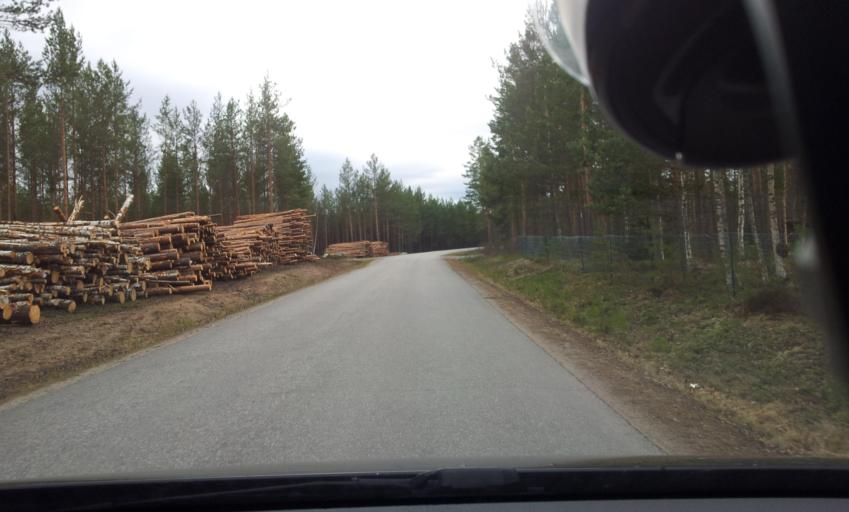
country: SE
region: Gaevleborg
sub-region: Ljusdals Kommun
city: Ljusdal
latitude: 61.8343
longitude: 16.0192
